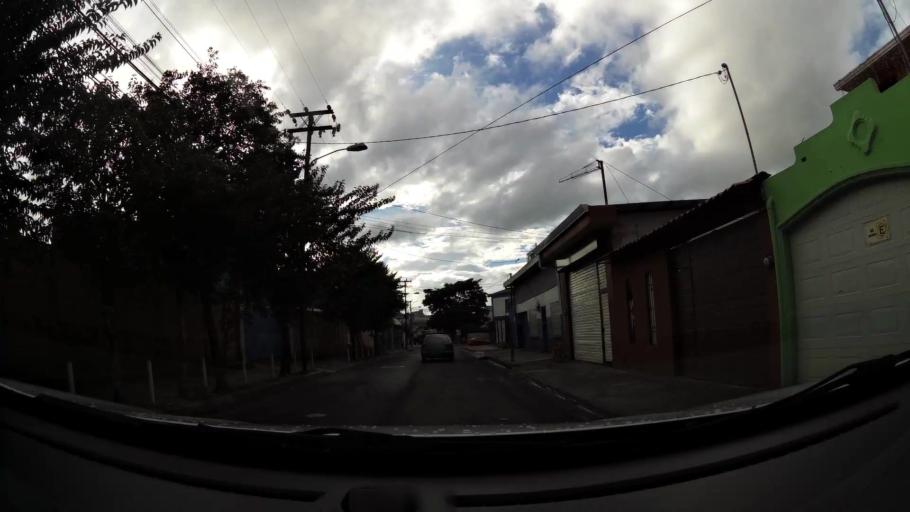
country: CR
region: San Jose
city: San Jose
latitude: 9.9401
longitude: -84.0887
